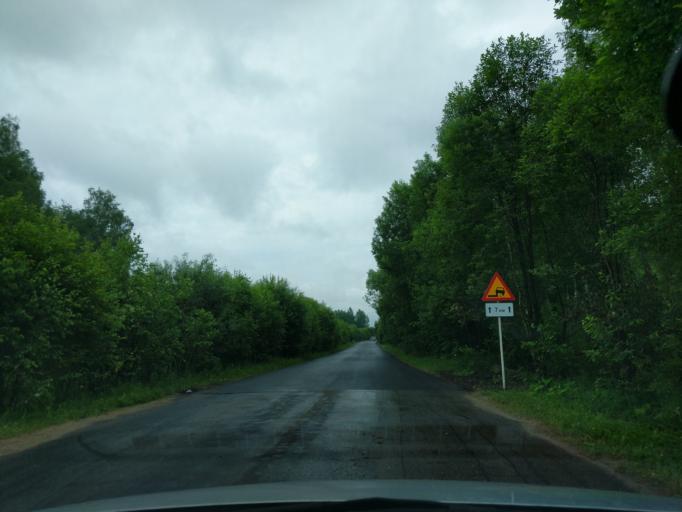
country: RU
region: Kaluga
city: Myatlevo
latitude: 54.8054
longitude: 35.7006
